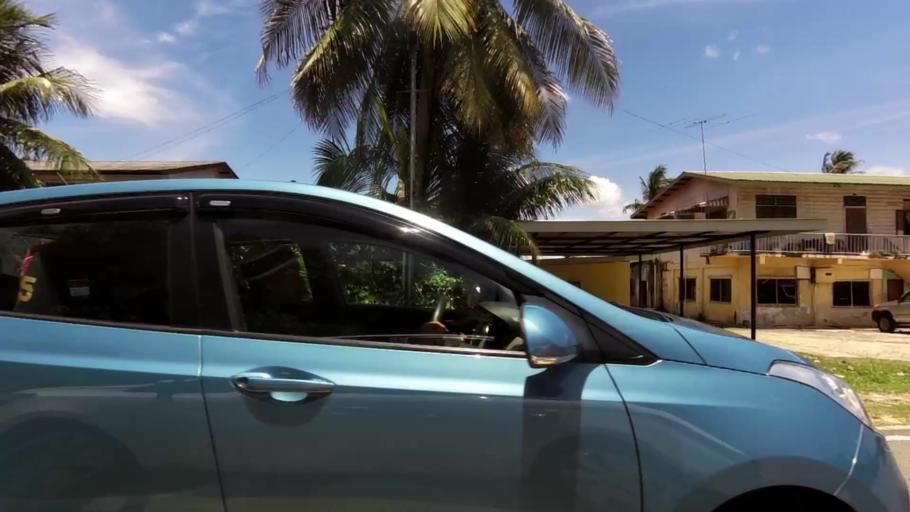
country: BN
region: Brunei and Muara
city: Bandar Seri Begawan
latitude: 4.9279
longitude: 114.9314
